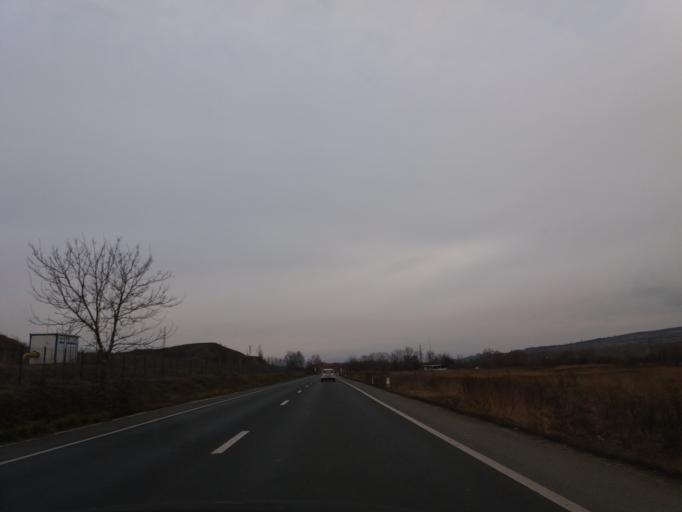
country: RO
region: Hunedoara
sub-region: Comuna Calan
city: Calan
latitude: 45.7465
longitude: 23.0002
